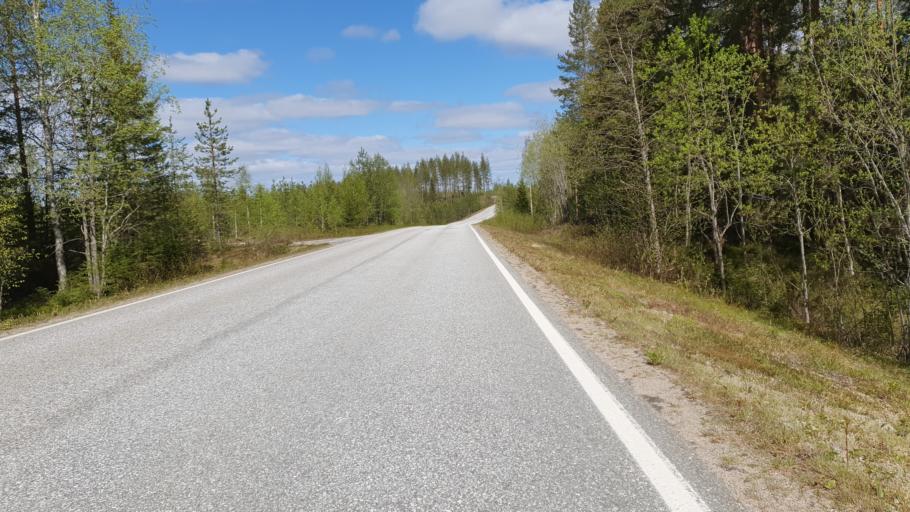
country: FI
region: Kainuu
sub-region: Kehys-Kainuu
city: Kuhmo
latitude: 64.3635
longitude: 29.4888
